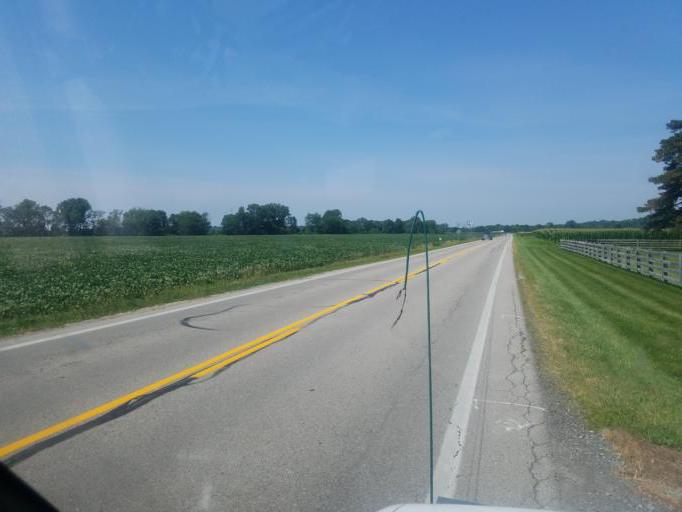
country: US
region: Ohio
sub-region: Logan County
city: West Liberty
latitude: 40.2508
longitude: -83.7318
